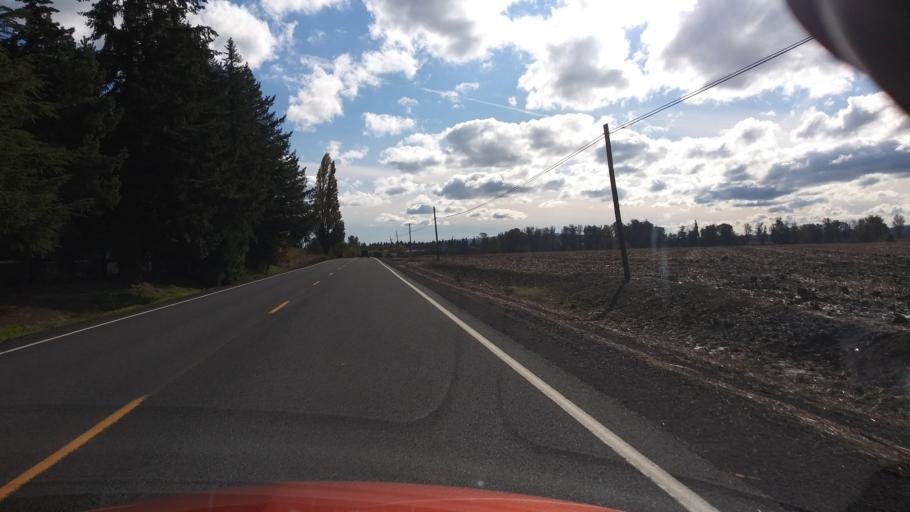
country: US
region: Oregon
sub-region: Washington County
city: Banks
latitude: 45.5788
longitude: -123.1118
